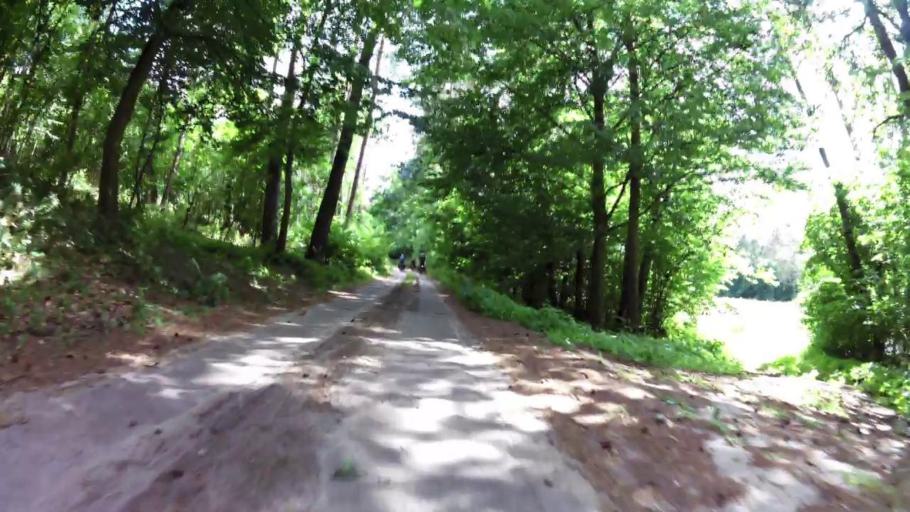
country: PL
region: West Pomeranian Voivodeship
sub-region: Powiat lobeski
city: Lobez
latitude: 53.6462
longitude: 15.5813
